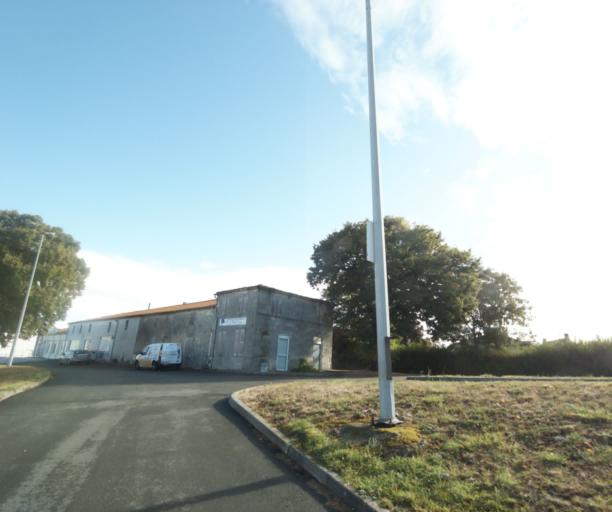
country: FR
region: Poitou-Charentes
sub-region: Departement de la Charente-Maritime
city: Tonnay-Charente
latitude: 45.9499
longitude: -0.9334
